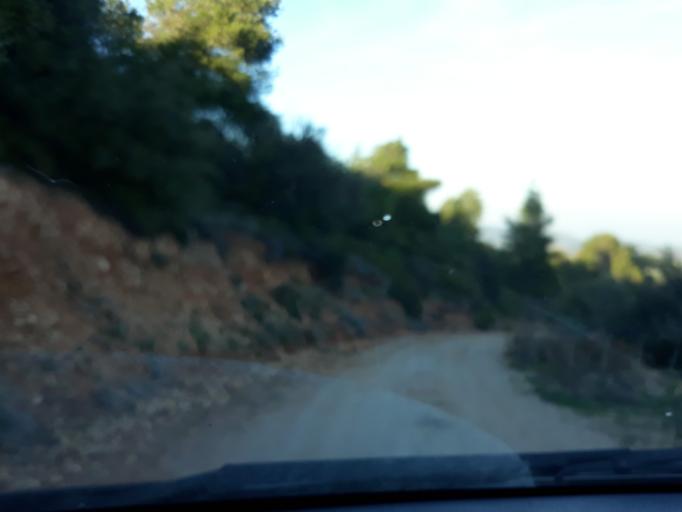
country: GR
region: Central Greece
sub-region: Nomos Voiotias
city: Asopia
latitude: 38.2757
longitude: 23.5297
